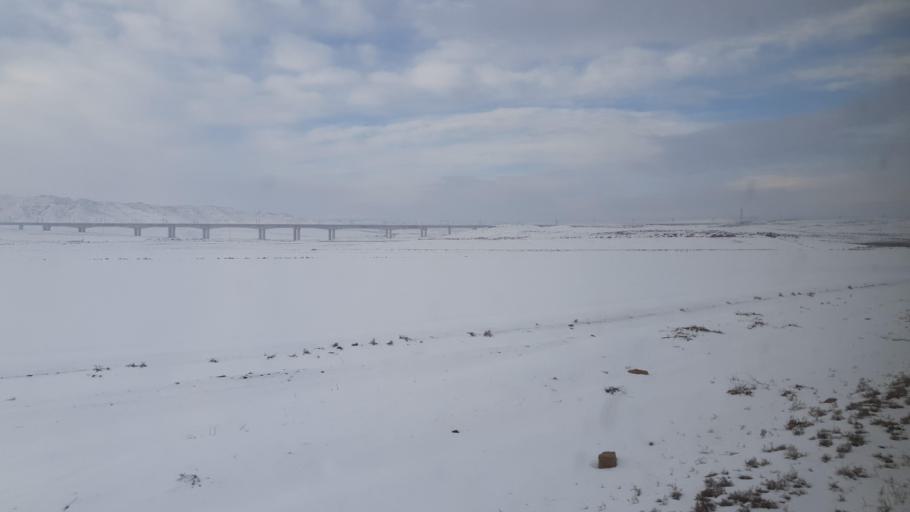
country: TR
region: Kirikkale
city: Delice
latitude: 39.8950
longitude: 33.9874
